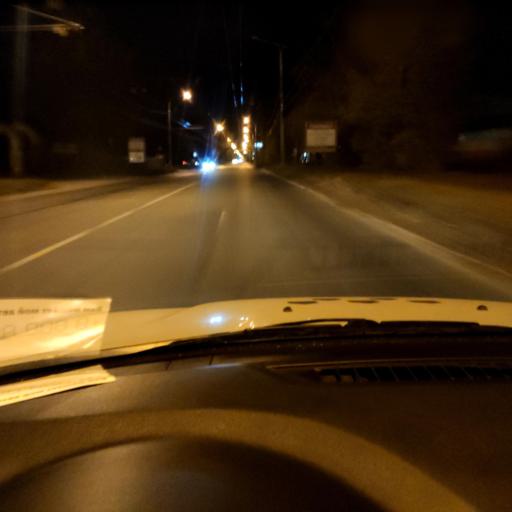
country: RU
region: Samara
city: Tol'yatti
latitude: 53.5504
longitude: 49.4486
